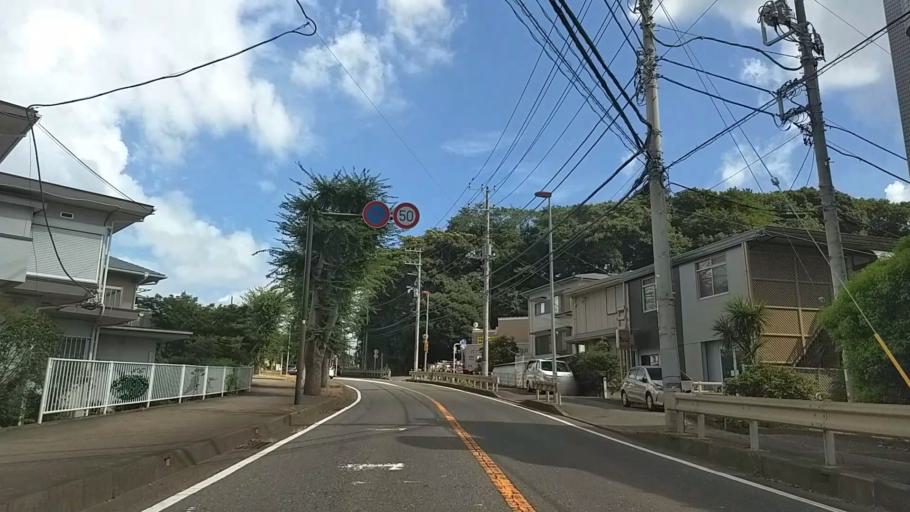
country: JP
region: Kanagawa
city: Miura
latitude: 35.1846
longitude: 139.6293
